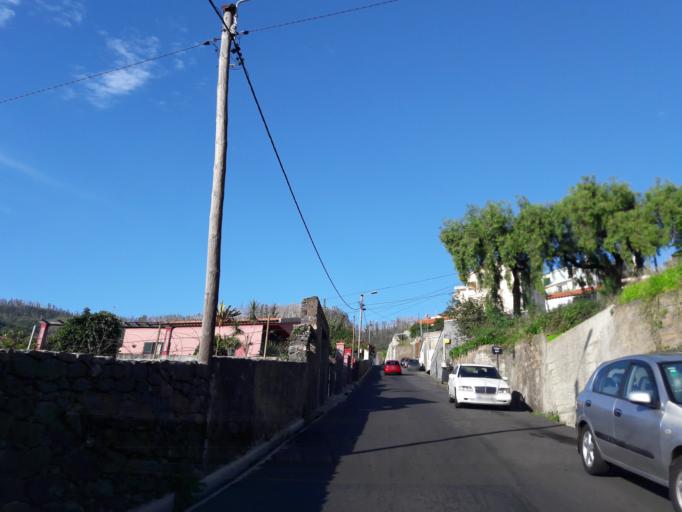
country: PT
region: Madeira
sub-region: Funchal
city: Nossa Senhora do Monte
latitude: 32.6731
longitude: -16.9209
